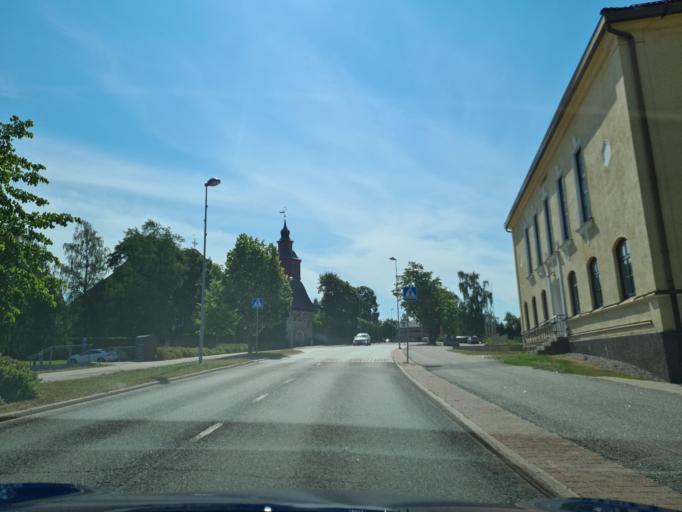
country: FI
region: Varsinais-Suomi
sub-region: Turku
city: Paimio
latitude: 60.4555
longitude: 22.6910
